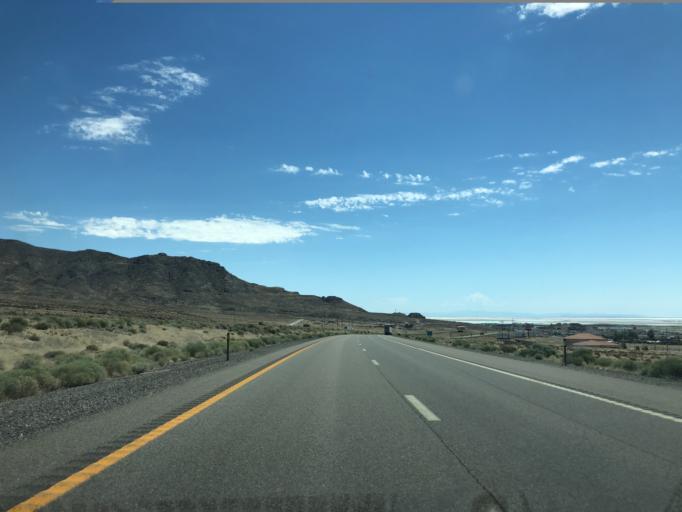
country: US
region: Nevada
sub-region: Elko County
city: West Wendover
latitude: 40.7445
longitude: -114.0783
